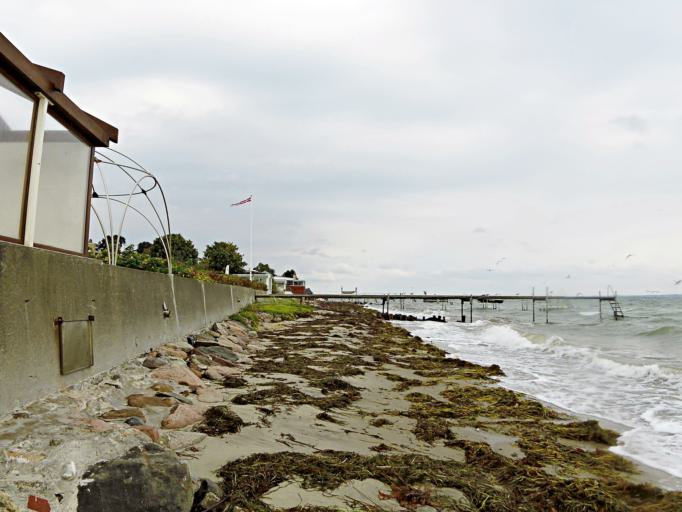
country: DK
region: Capital Region
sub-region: Rudersdal Kommune
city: Trorod
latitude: 55.8217
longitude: 12.5753
